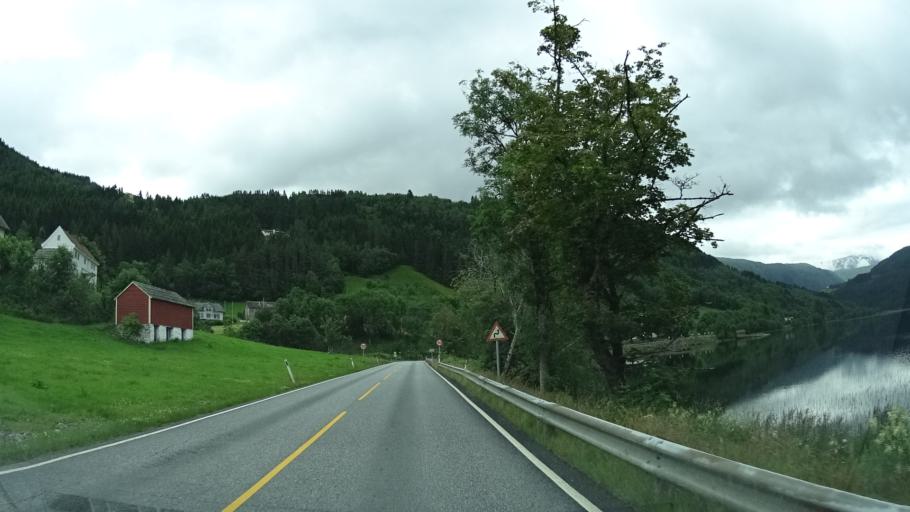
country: NO
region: Hordaland
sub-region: Granvin
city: Granvin
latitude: 60.5577
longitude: 6.7300
